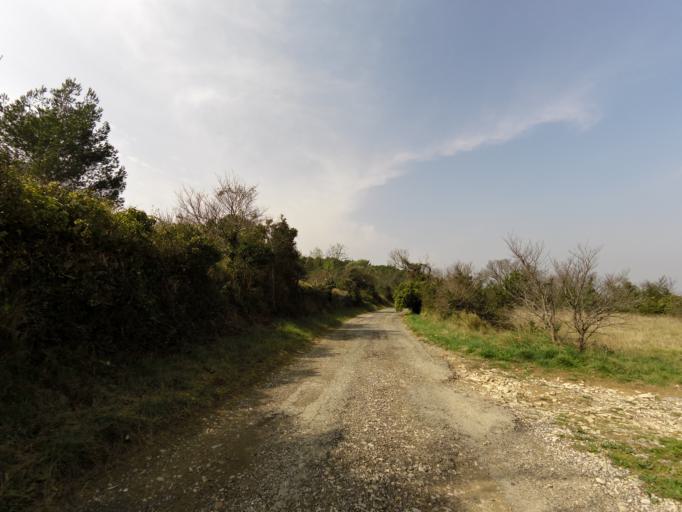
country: FR
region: Languedoc-Roussillon
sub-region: Departement du Gard
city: Congenies
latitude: 43.7662
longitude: 4.1611
